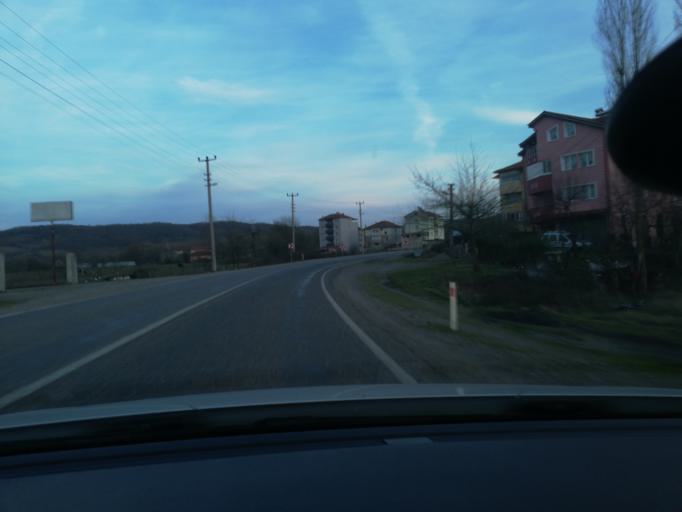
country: TR
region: Zonguldak
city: Saltukova
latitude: 41.5271
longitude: 32.0991
